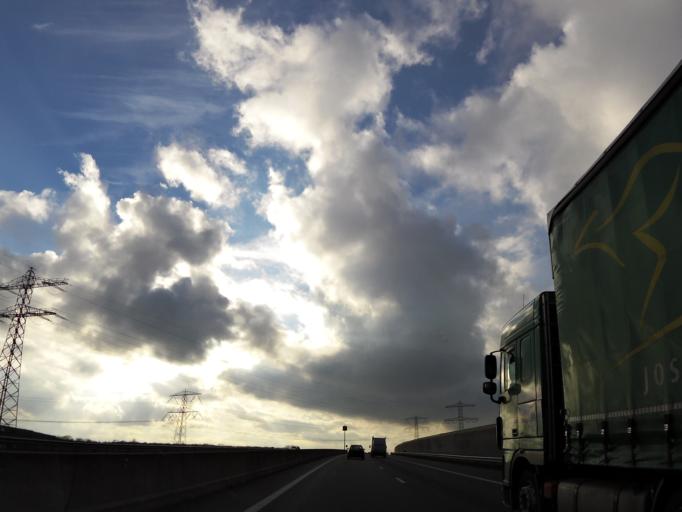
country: NL
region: Limburg
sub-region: Gemeente Roerdalen
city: Montfort
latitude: 51.1478
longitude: 5.9383
